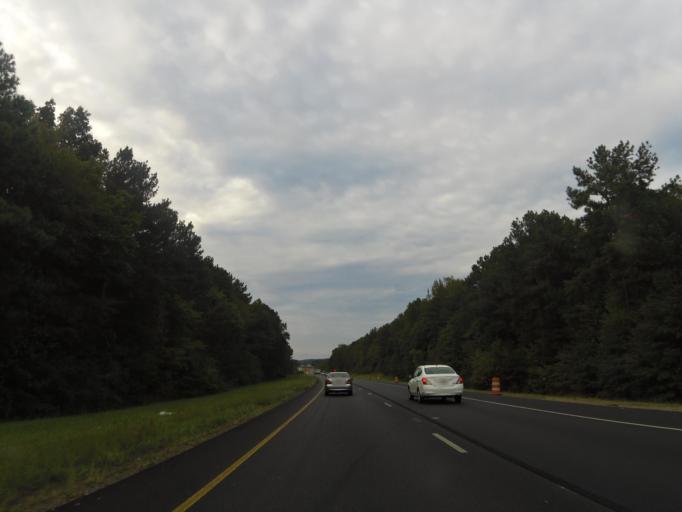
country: US
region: Alabama
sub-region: Shelby County
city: Alabaster
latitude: 33.2492
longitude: -86.7985
